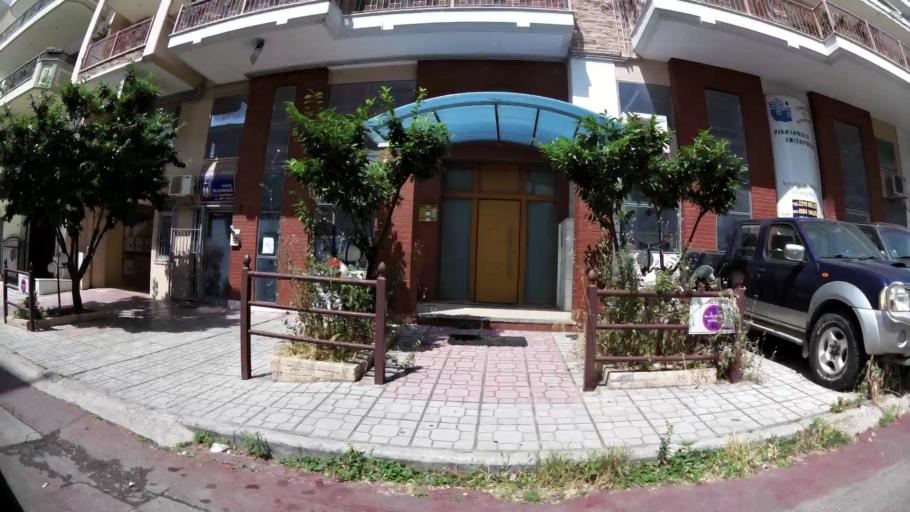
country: GR
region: Central Macedonia
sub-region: Nomos Thessalonikis
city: Evosmos
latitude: 40.6761
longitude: 22.9203
